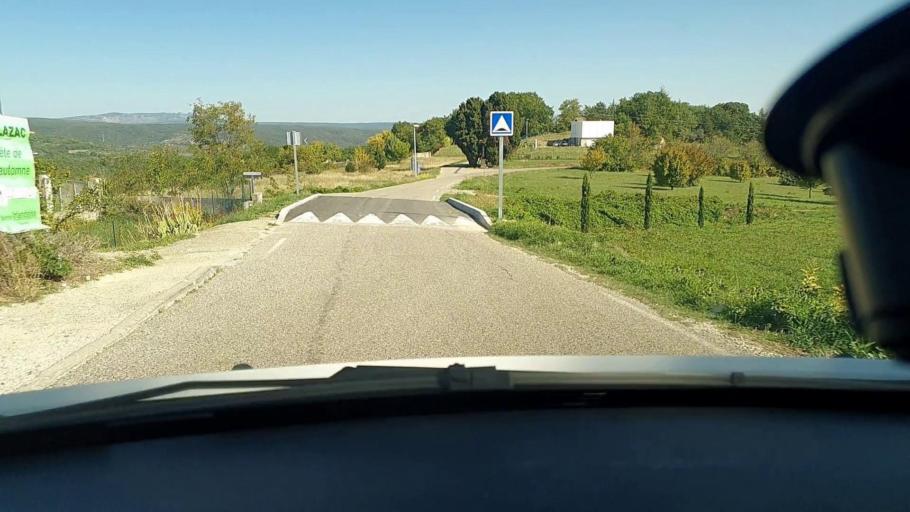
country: FR
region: Languedoc-Roussillon
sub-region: Departement du Gard
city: Saint-Julien-de-Peyrolas
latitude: 44.2612
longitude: 4.5258
